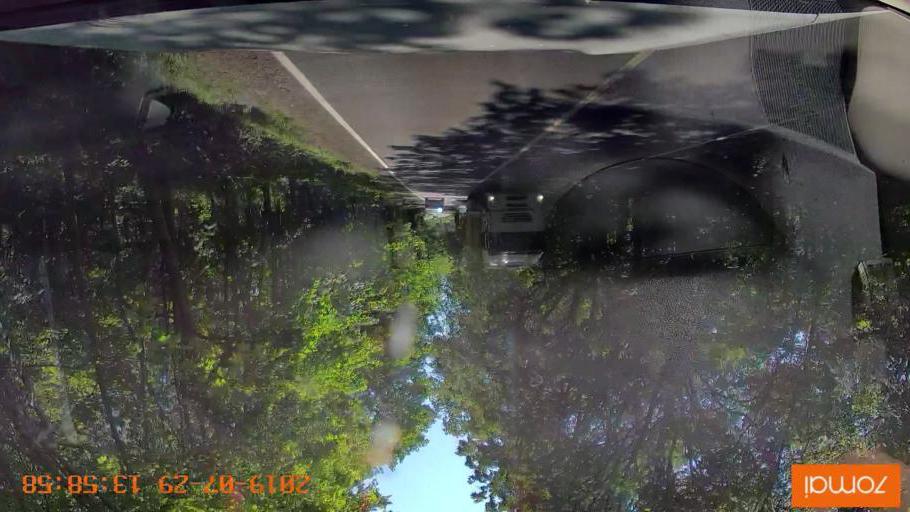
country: RU
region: Kaliningrad
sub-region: Gorod Kaliningrad
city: Baltiysk
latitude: 54.6885
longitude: 19.9349
